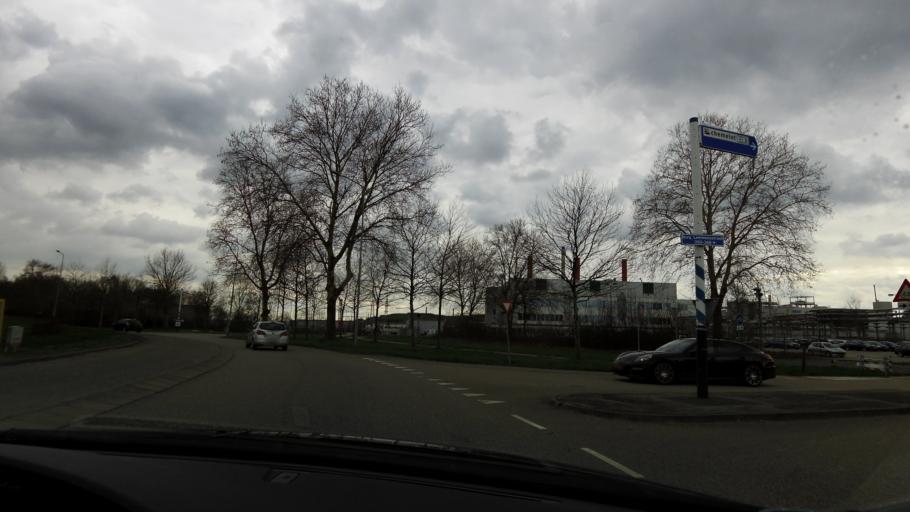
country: NL
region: Limburg
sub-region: Gemeente Stein
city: Urmond
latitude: 50.9840
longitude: 5.8045
